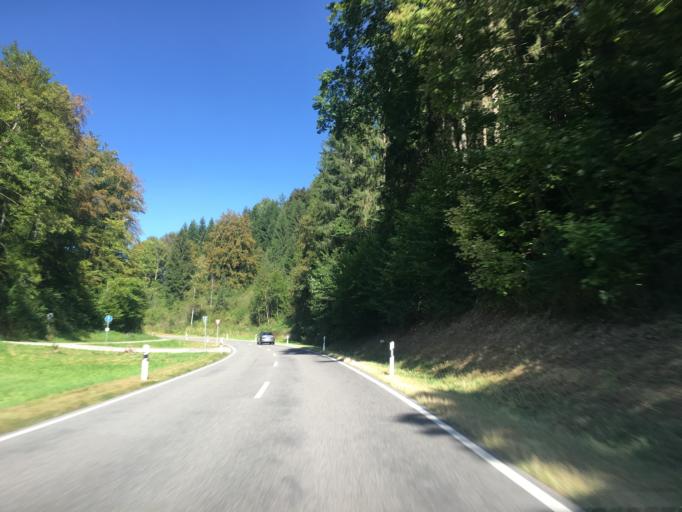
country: DE
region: Baden-Wuerttemberg
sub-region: Tuebingen Region
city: Munsingen
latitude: 48.3676
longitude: 9.4826
